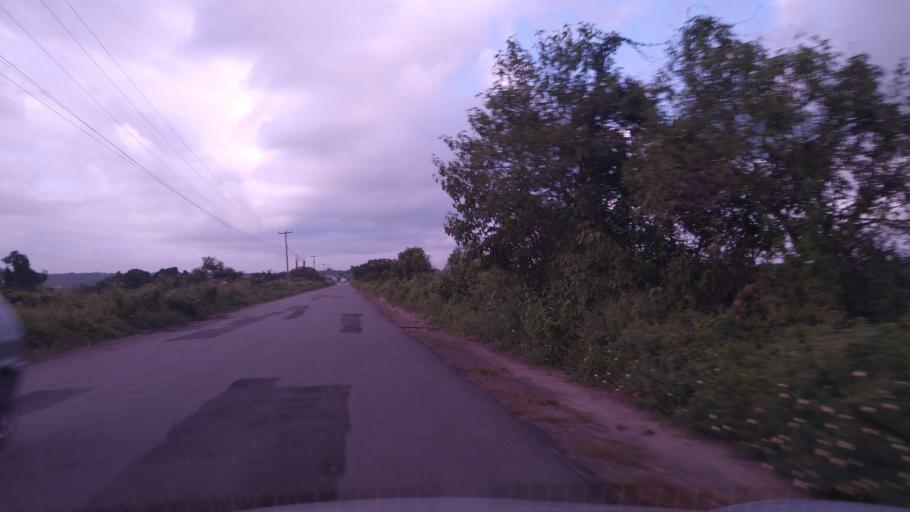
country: BR
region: Ceara
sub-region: Chorozinho
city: Chorozinho
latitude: -4.3070
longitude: -38.4982
